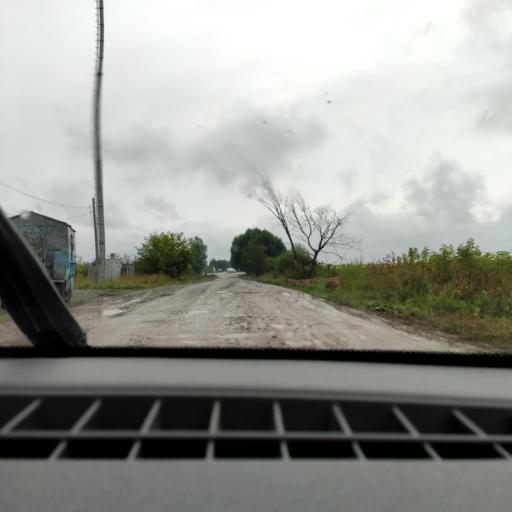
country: RU
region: Bashkortostan
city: Avdon
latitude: 54.7179
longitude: 55.7723
